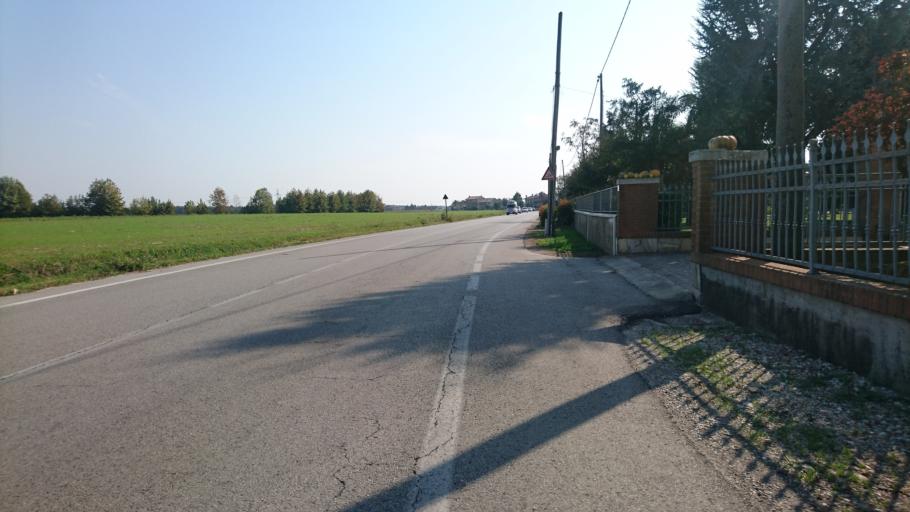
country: IT
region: Veneto
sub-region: Provincia di Vicenza
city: Grumolo delle Abbadesse
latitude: 45.5435
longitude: 11.6689
